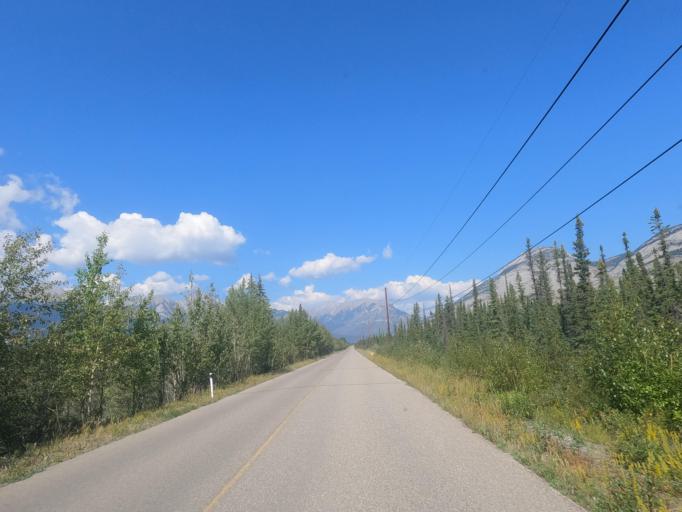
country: CA
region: Alberta
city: Jasper Park Lodge
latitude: 53.0001
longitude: -118.0848
